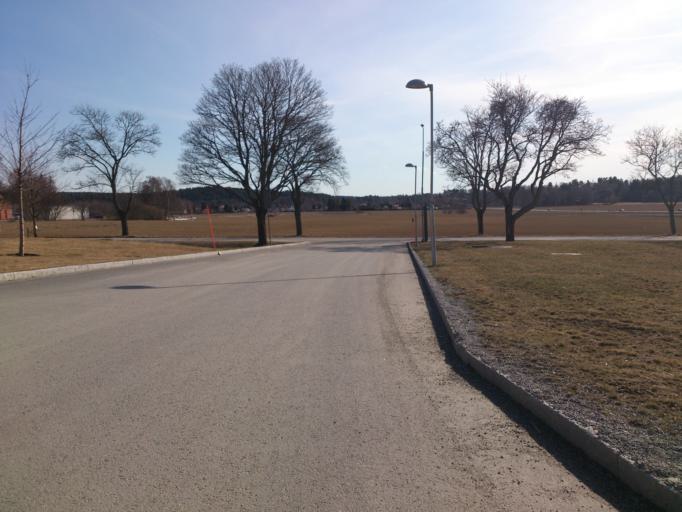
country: SE
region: Uppsala
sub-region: Uppsala Kommun
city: Saevja
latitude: 59.8140
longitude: 17.6541
